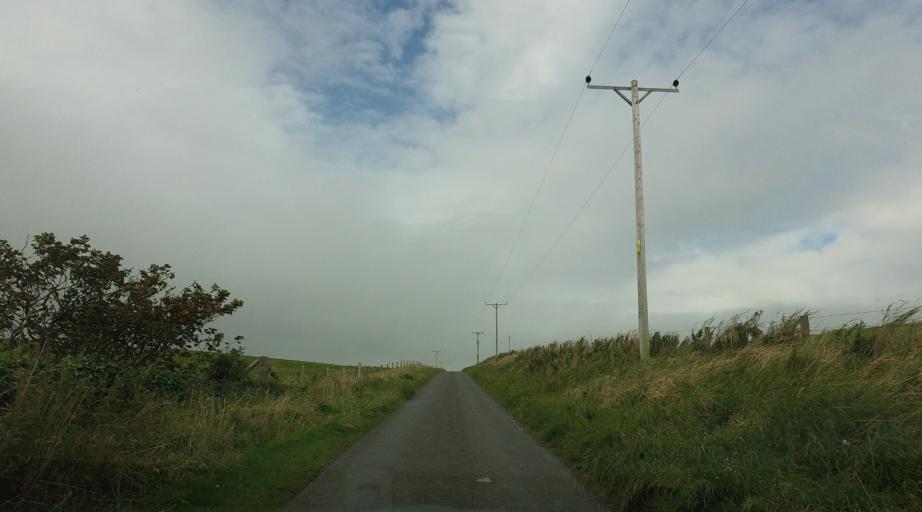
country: GB
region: Scotland
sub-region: Orkney Islands
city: Kirkwall
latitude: 58.8069
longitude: -2.9253
